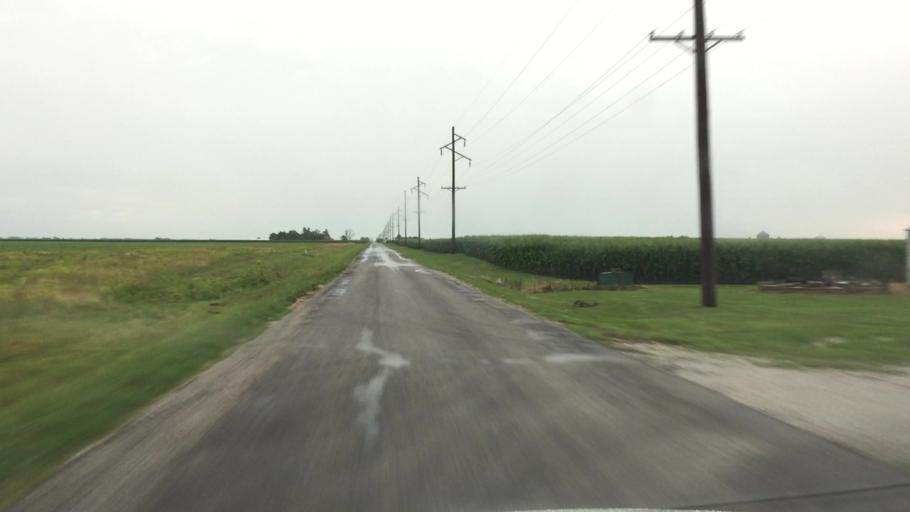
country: US
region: Illinois
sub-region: Hancock County
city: Nauvoo
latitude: 40.5177
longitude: -91.2692
